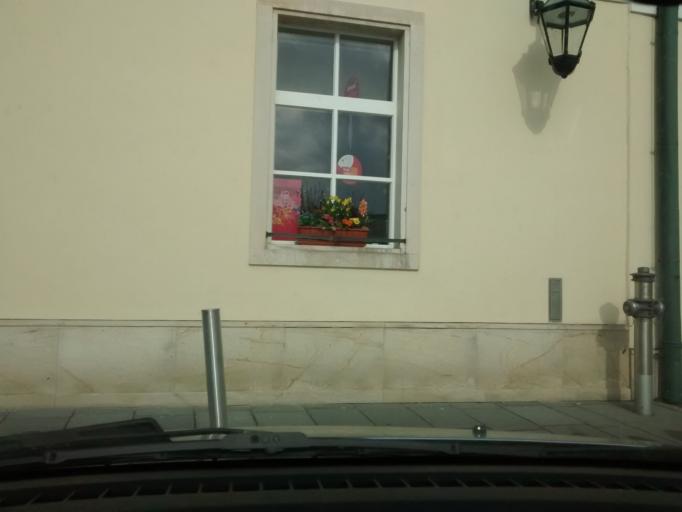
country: AT
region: Lower Austria
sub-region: Politischer Bezirk Modling
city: Laxenburg
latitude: 48.0679
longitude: 16.3573
